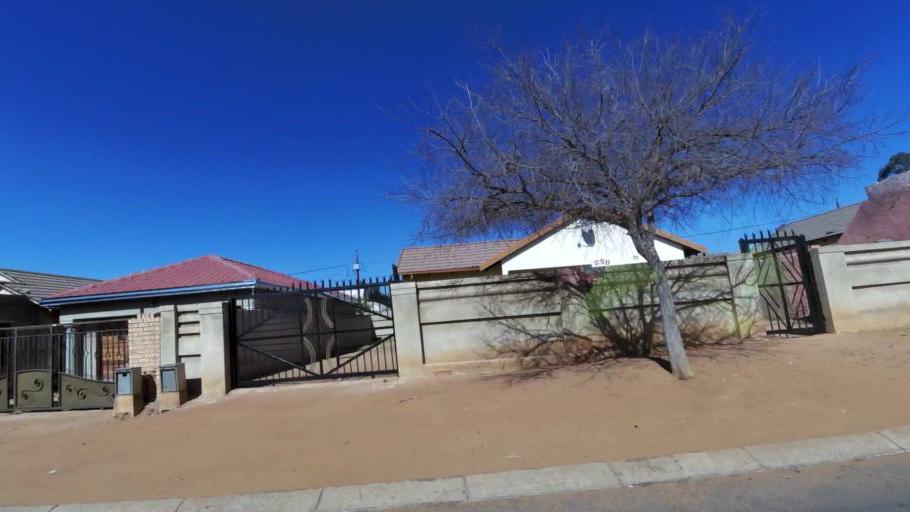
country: ZA
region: Gauteng
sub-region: City of Johannesburg Metropolitan Municipality
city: Johannesburg
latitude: -26.2498
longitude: 27.9814
